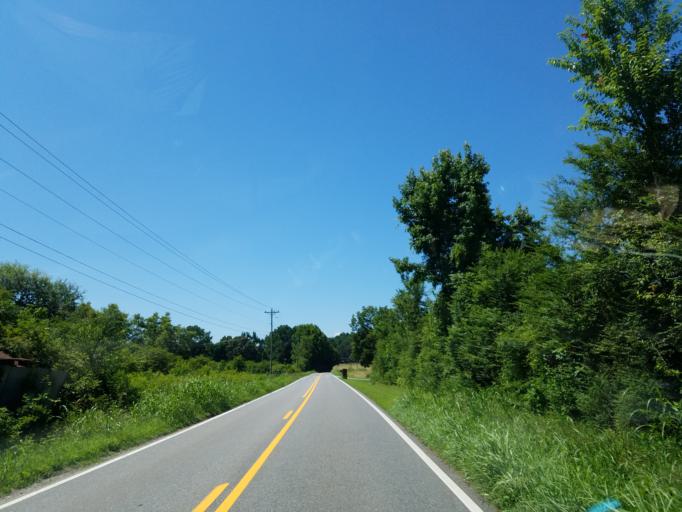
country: US
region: Georgia
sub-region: Forsyth County
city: Cumming
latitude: 34.2636
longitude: -84.0723
